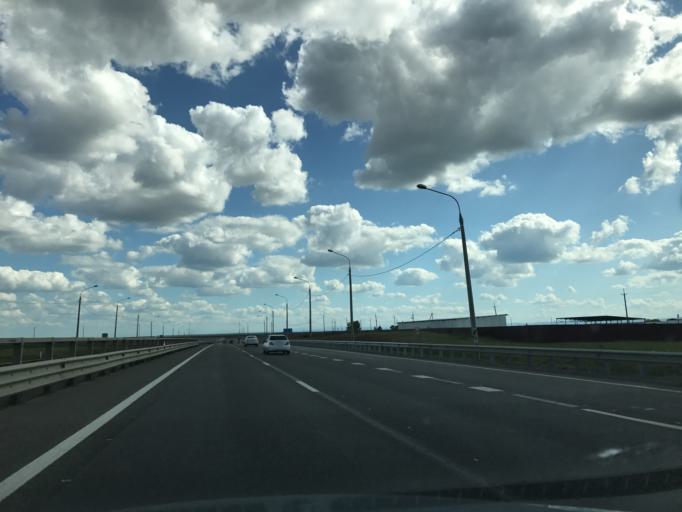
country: RU
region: Adygeya
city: Adygeysk
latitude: 44.8476
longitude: 39.2057
